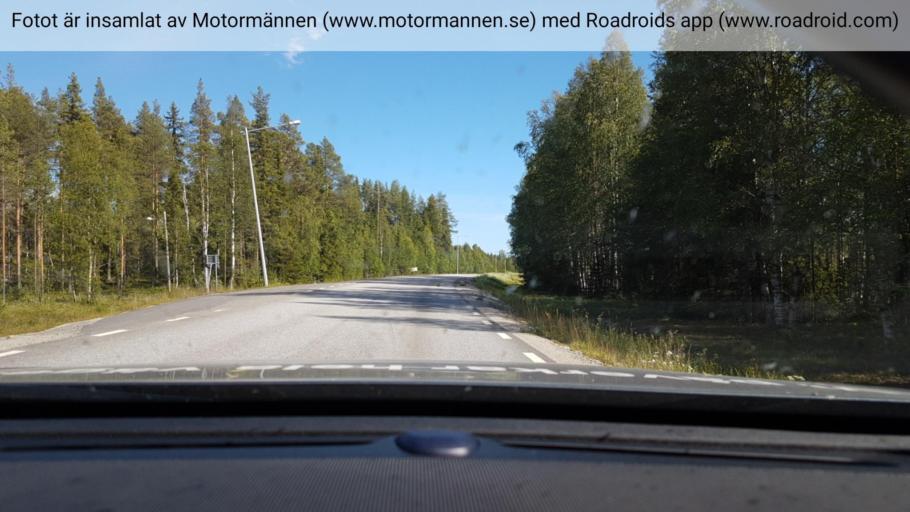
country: SE
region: Vaesterbotten
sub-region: Lycksele Kommun
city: Lycksele
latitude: 64.6913
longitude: 18.4016
